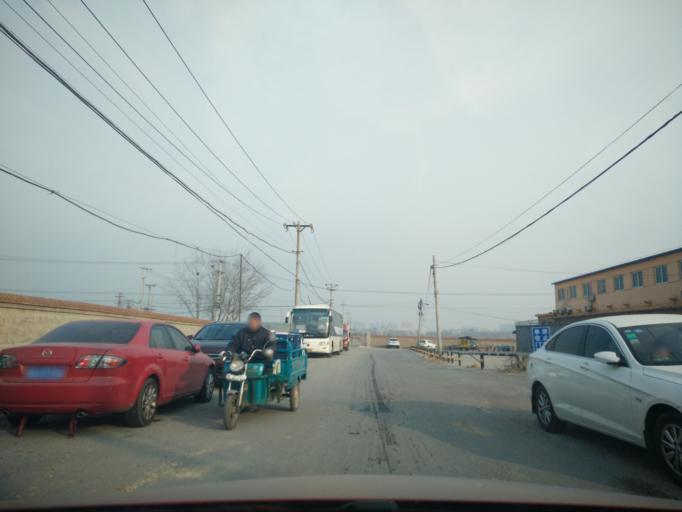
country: CN
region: Beijing
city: Jiugong
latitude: 39.7977
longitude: 116.4242
